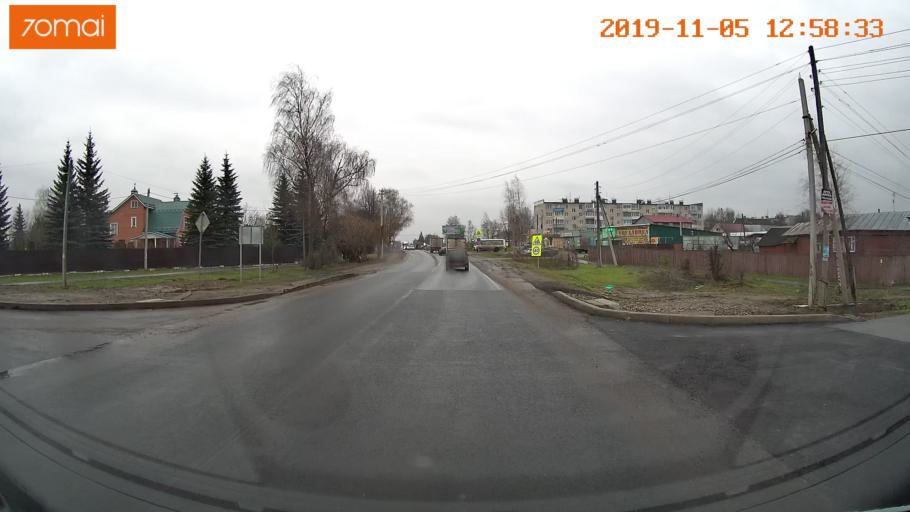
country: RU
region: Ivanovo
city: Kokhma
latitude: 56.9212
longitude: 41.1198
